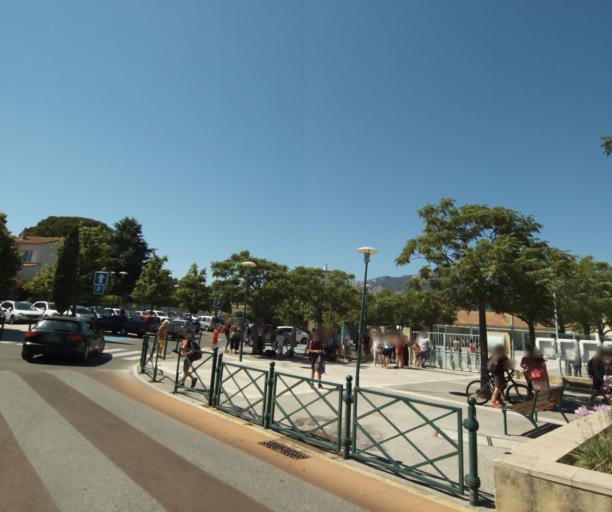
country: FR
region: Provence-Alpes-Cote d'Azur
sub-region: Departement du Var
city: La Garde
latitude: 43.1251
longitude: 6.0153
